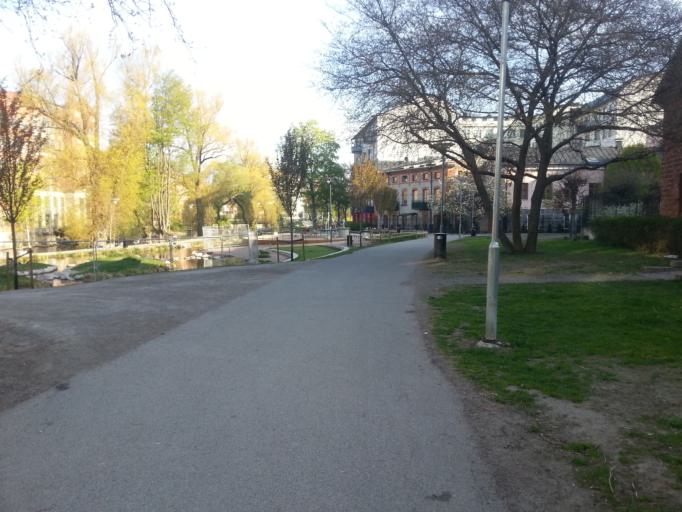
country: SE
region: OEstergoetland
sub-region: Norrkopings Kommun
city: Norrkoping
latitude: 58.5900
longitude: 16.1852
